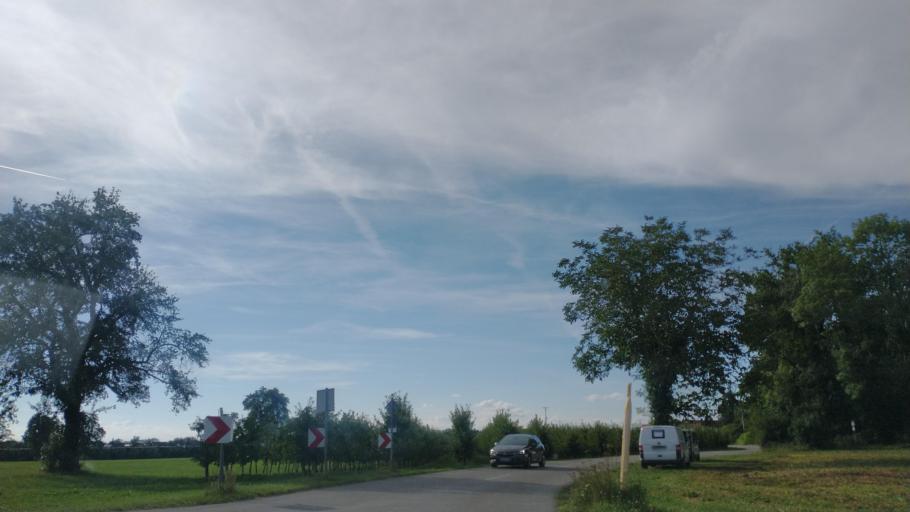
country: DE
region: Baden-Wuerttemberg
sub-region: Tuebingen Region
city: Kressbronn am Bodensee
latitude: 47.5921
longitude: 9.5772
